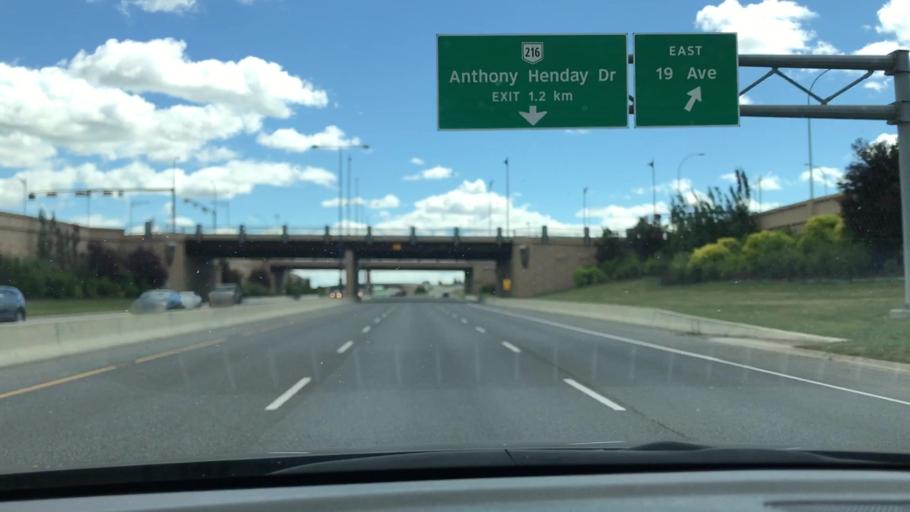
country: CA
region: Alberta
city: Edmonton
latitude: 53.4554
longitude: -113.4926
